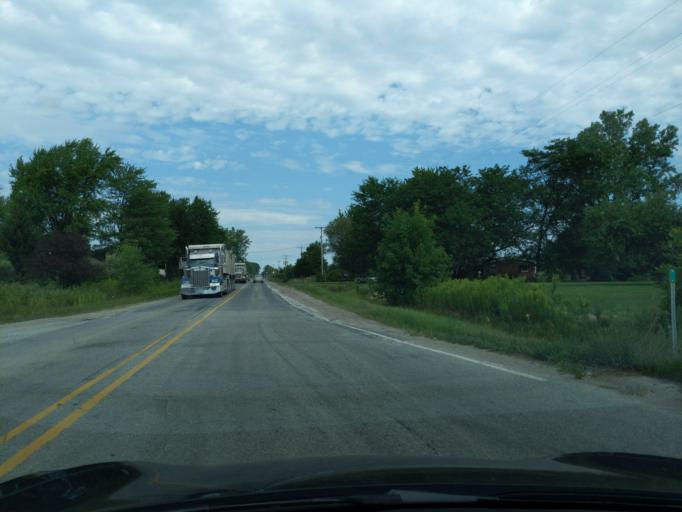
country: US
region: Michigan
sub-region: Gratiot County
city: Breckenridge
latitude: 43.4083
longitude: -84.3699
